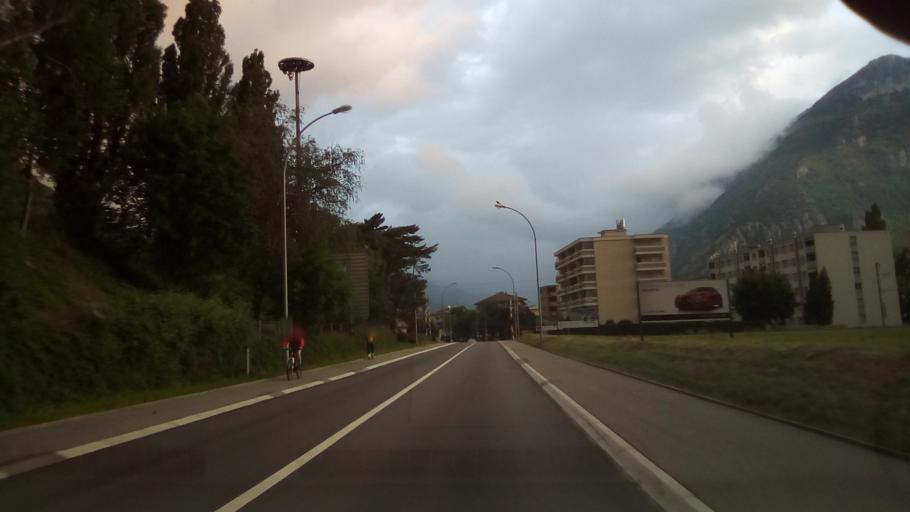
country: CH
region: Valais
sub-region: Martigny District
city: Martigny-Ville
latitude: 46.1003
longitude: 7.0823
